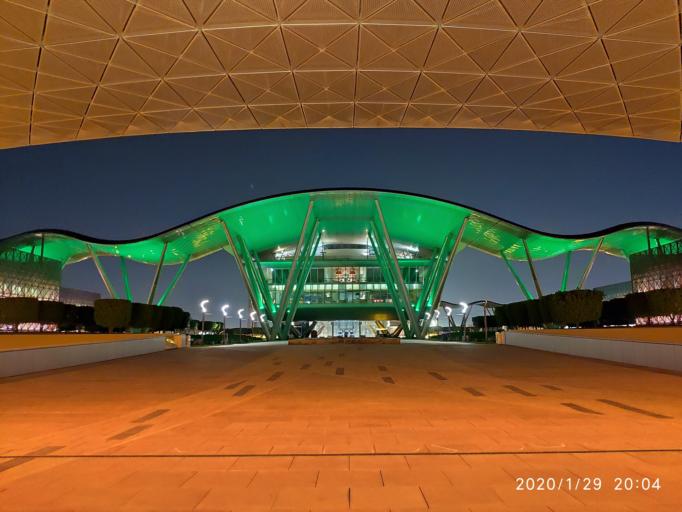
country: QA
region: Baladiyat ar Rayyan
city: Ar Rayyan
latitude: 25.3234
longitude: 51.4374
